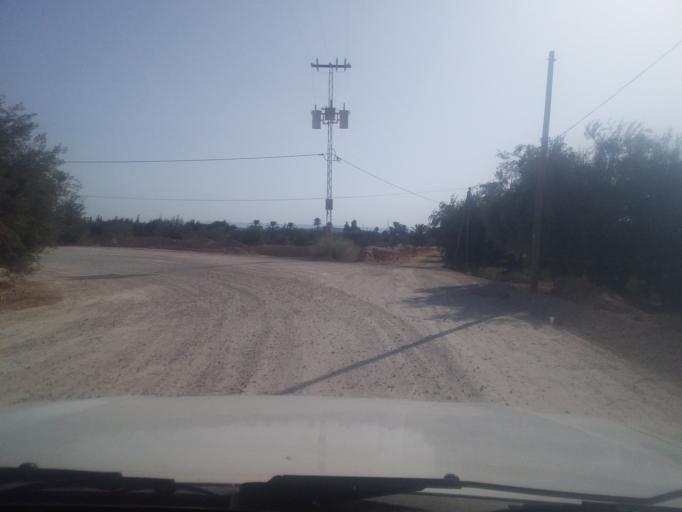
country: TN
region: Qabis
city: Matmata
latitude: 33.5978
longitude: 10.2735
